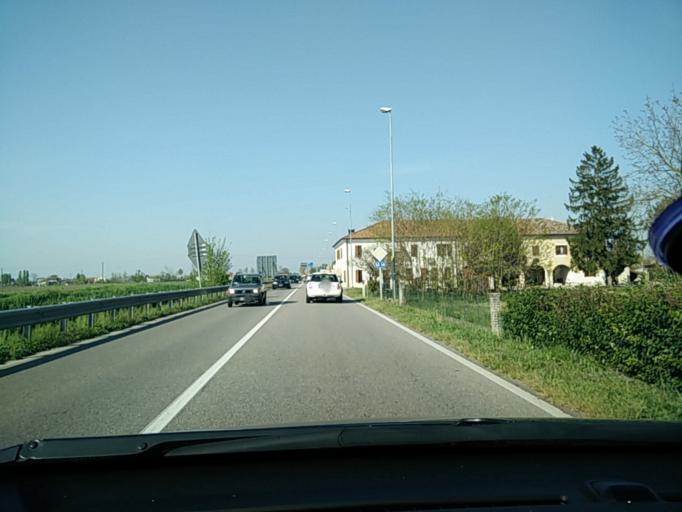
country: IT
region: Veneto
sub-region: Provincia di Venezia
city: Fossalta di Piave
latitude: 45.6149
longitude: 12.4928
